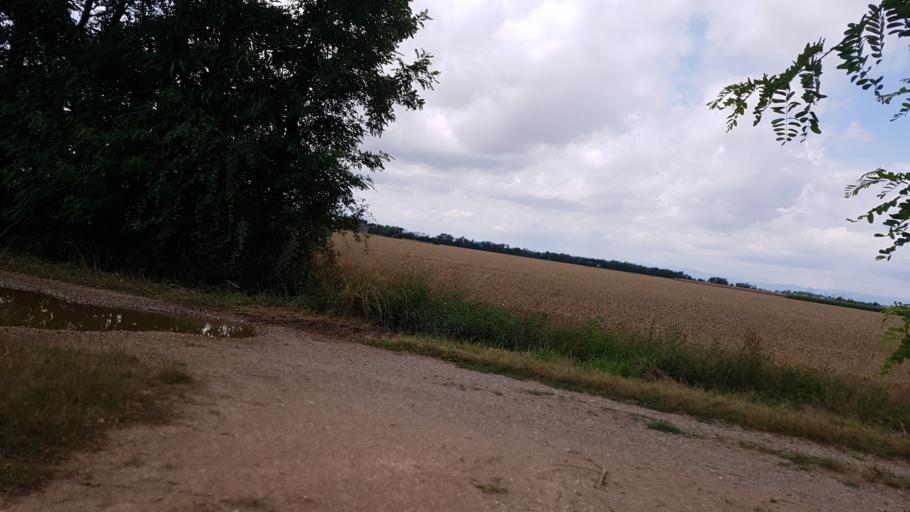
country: FR
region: Rhone-Alpes
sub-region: Departement du Rhone
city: Pusignan
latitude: 45.7295
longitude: 5.0676
